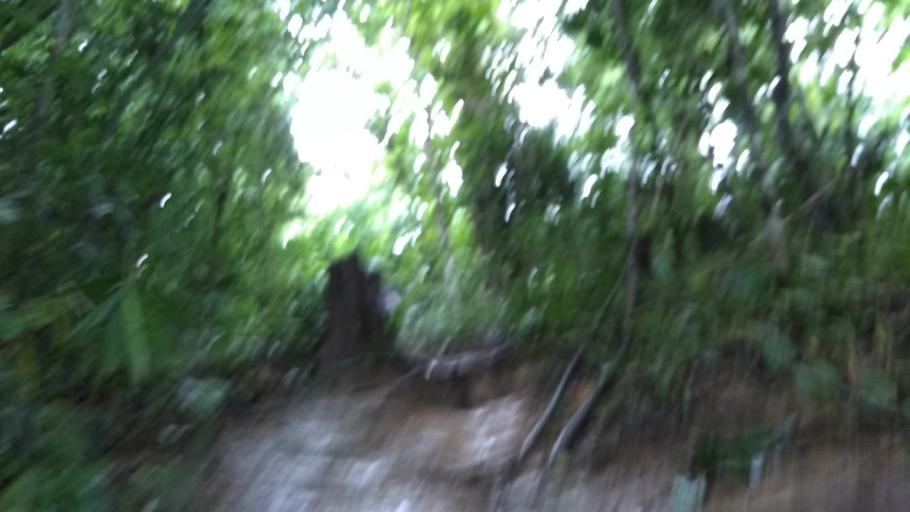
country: IN
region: Tripura
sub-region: Dhalai
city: Kamalpur
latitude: 24.1702
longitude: 91.8984
